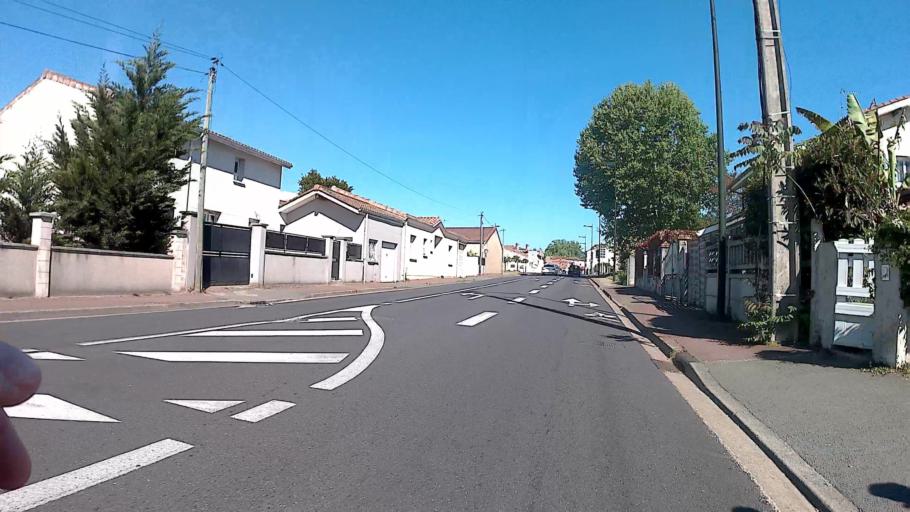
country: FR
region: Aquitaine
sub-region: Departement de la Gironde
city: Begles
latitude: 44.7986
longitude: -0.5415
